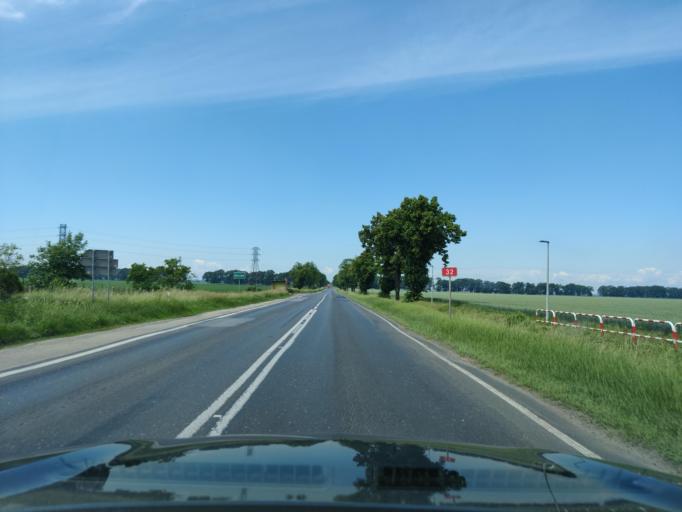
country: PL
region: Greater Poland Voivodeship
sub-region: Powiat grodziski
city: Granowo
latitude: 52.2244
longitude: 16.4862
